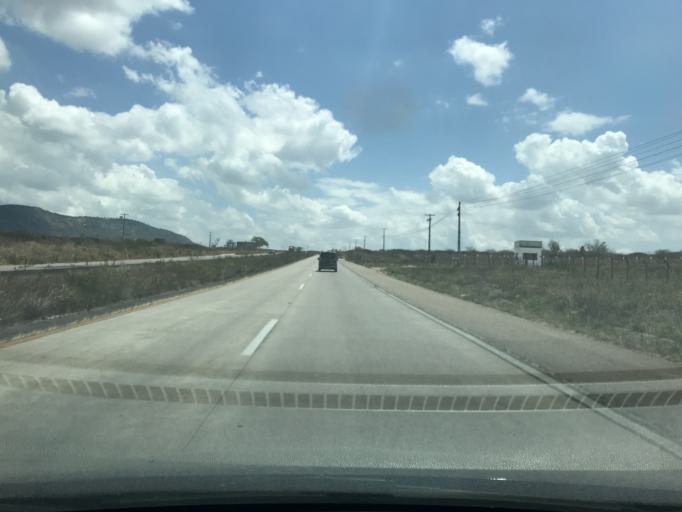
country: BR
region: Pernambuco
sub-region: Bezerros
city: Bezerros
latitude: -8.2912
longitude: -35.8228
